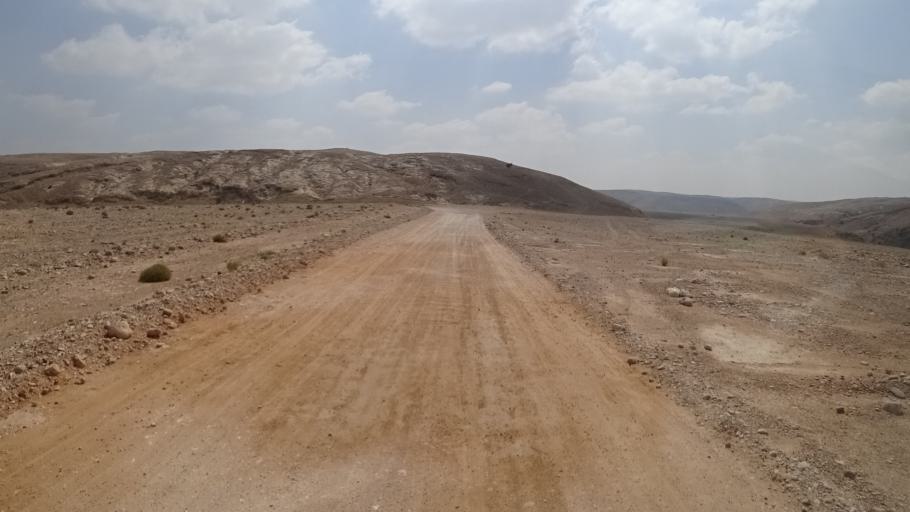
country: OM
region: Zufar
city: Salalah
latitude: 17.2369
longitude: 53.8967
